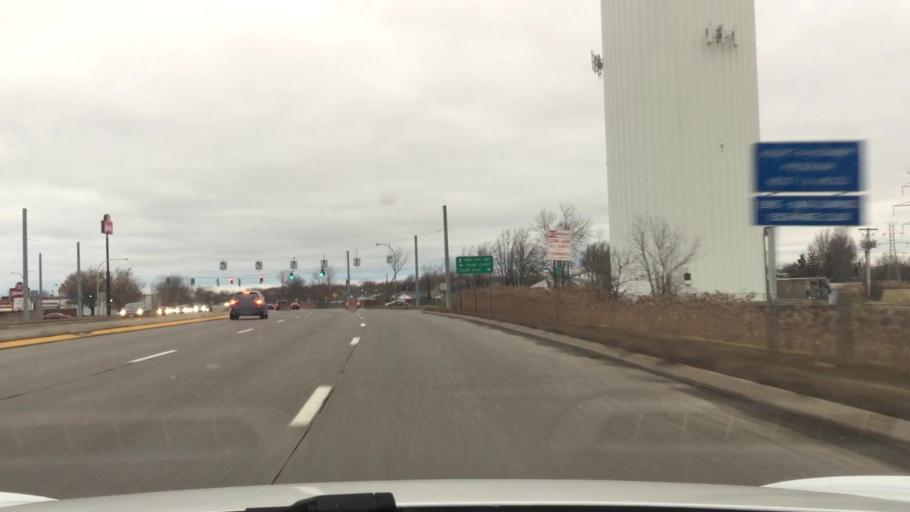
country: US
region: New York
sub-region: Erie County
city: Tonawanda
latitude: 43.0013
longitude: -78.8537
